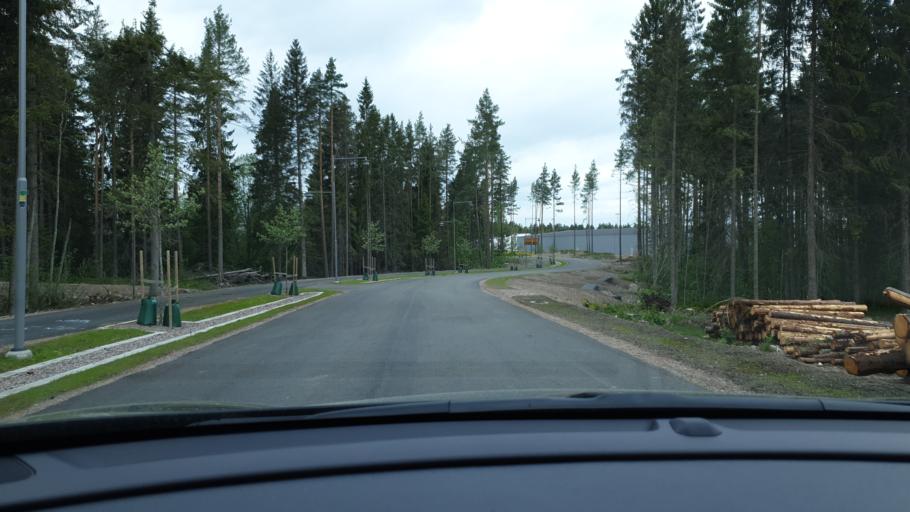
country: SE
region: Gaevleborg
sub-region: Gavle Kommun
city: Gavle
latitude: 60.6423
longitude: 17.1499
